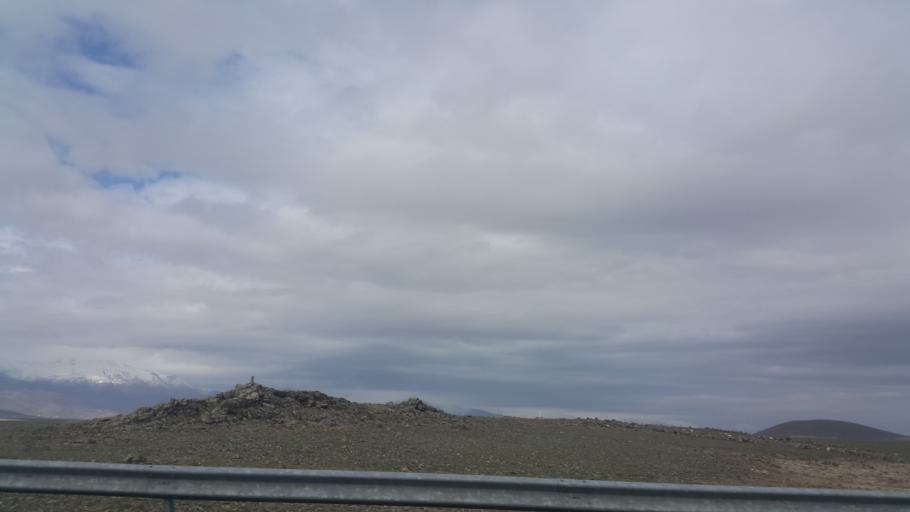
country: TR
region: Aksaray
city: Taspinar
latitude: 37.9846
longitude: 34.0703
